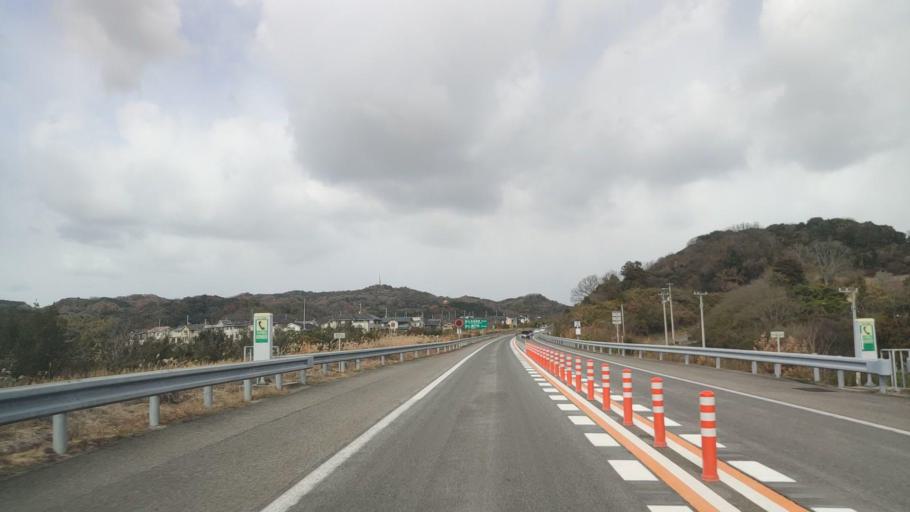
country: JP
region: Ehime
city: Hojo
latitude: 34.0650
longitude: 132.9733
